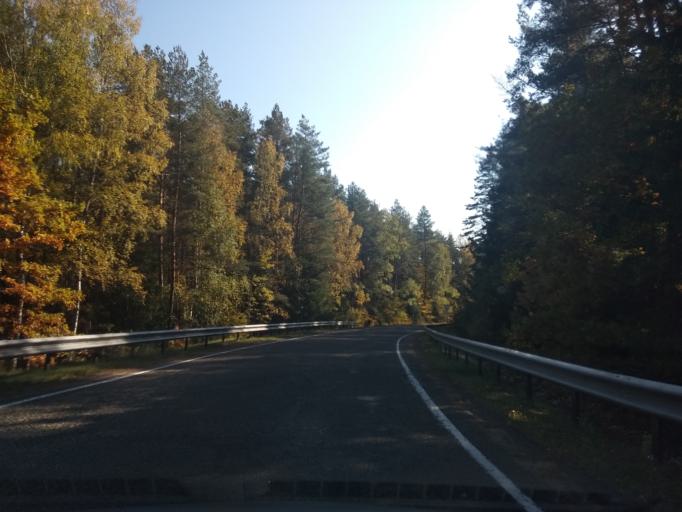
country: BY
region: Brest
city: Ivatsevichy
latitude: 52.8551
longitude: 25.6413
